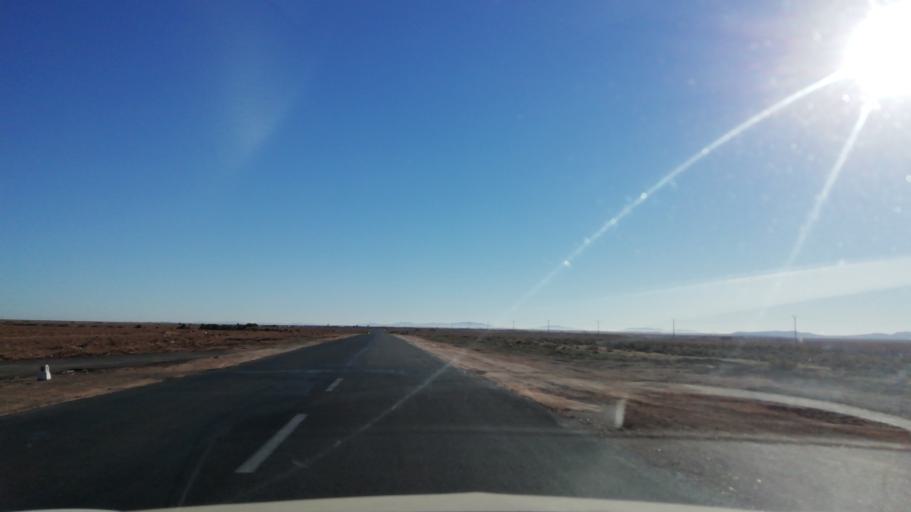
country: DZ
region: El Bayadh
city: El Bayadh
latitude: 33.8563
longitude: 0.5910
